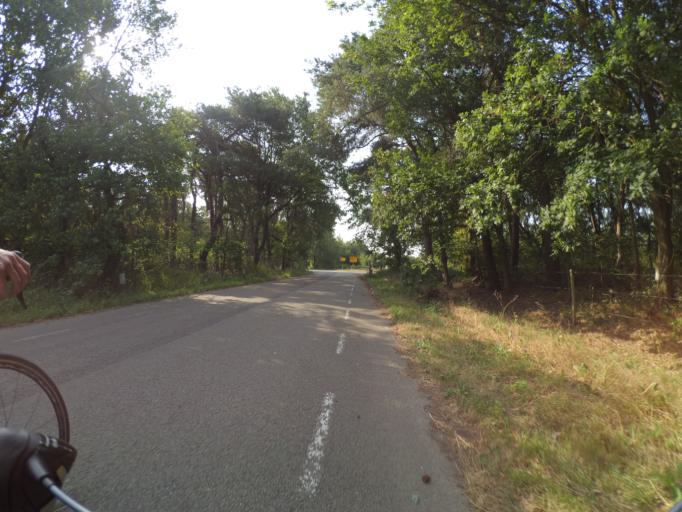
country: NL
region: North Brabant
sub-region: Gemeente Loon op Zand
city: Loon op Zand
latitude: 51.6112
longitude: 5.0598
